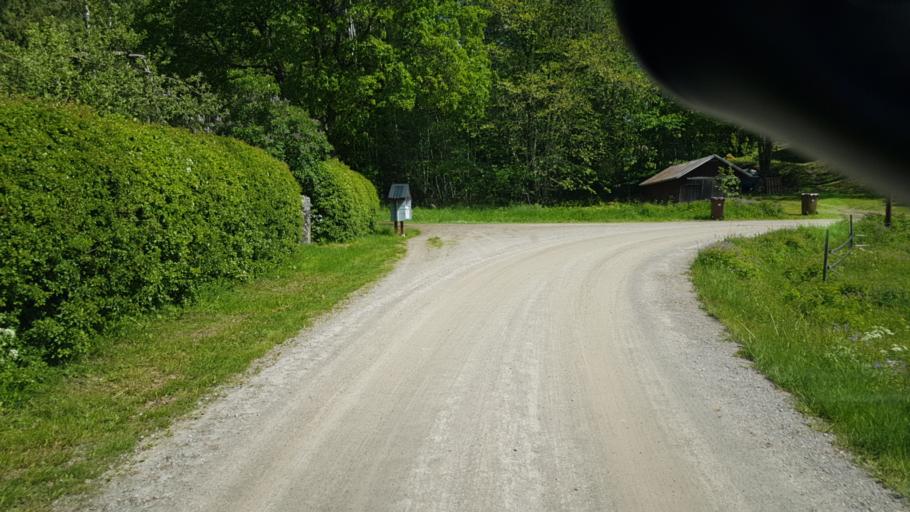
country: SE
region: Vaermland
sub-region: Sunne Kommun
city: Sunne
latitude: 59.7061
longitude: 12.8848
